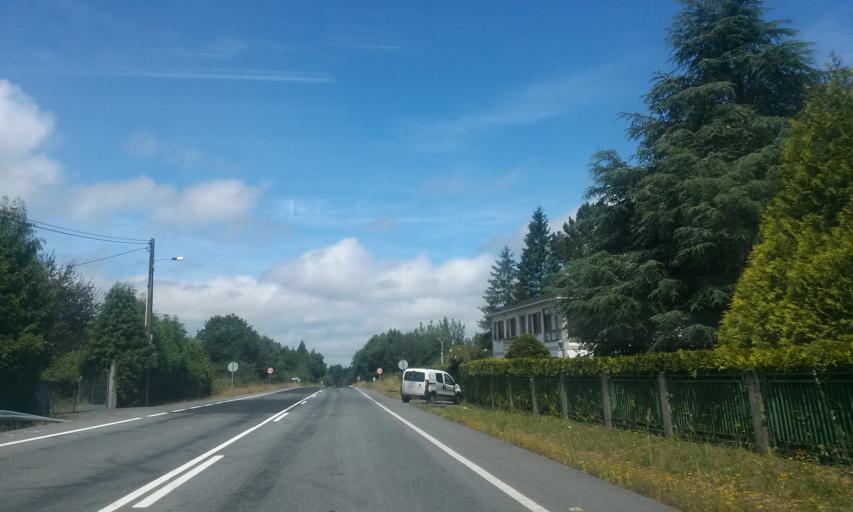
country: ES
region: Galicia
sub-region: Provincia de Lugo
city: Outeiro de Rei
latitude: 43.0212
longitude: -7.6778
